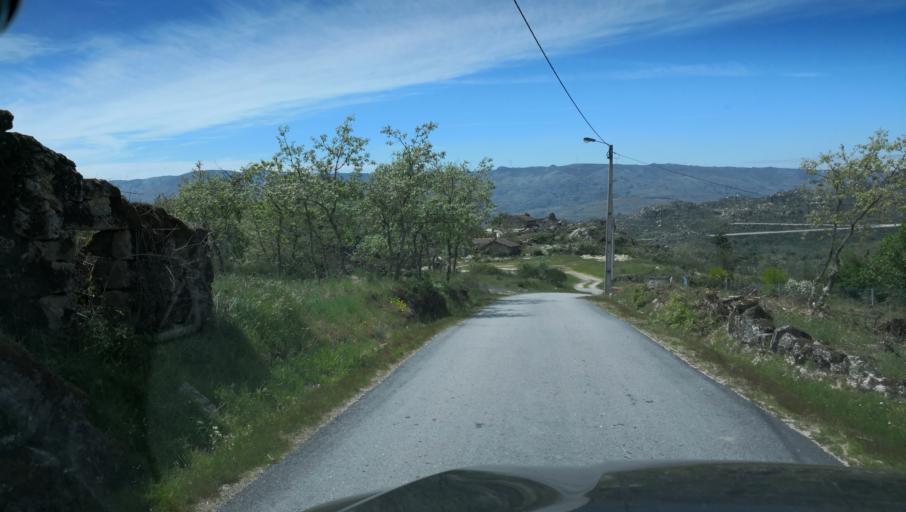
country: PT
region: Vila Real
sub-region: Vila Real
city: Vila Real
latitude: 41.3624
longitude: -7.6697
